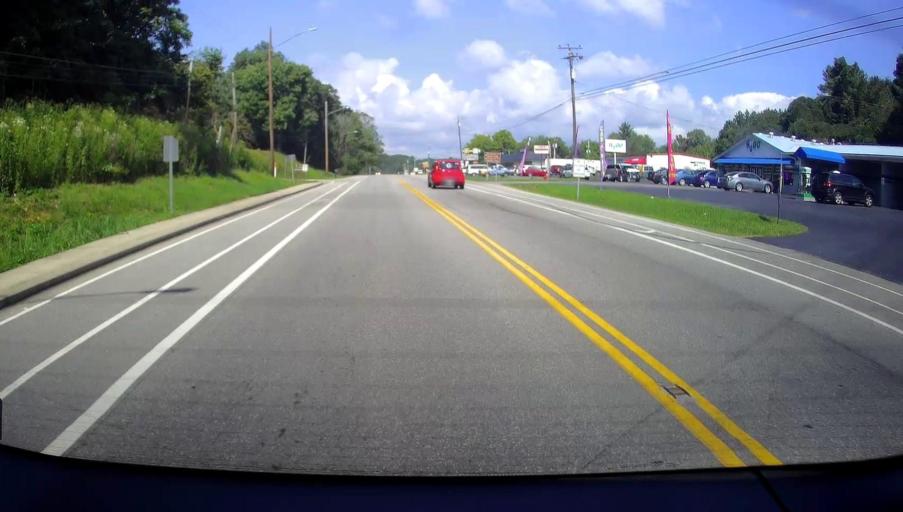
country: US
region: Tennessee
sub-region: Coffee County
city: Manchester
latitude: 35.4905
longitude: -86.0963
